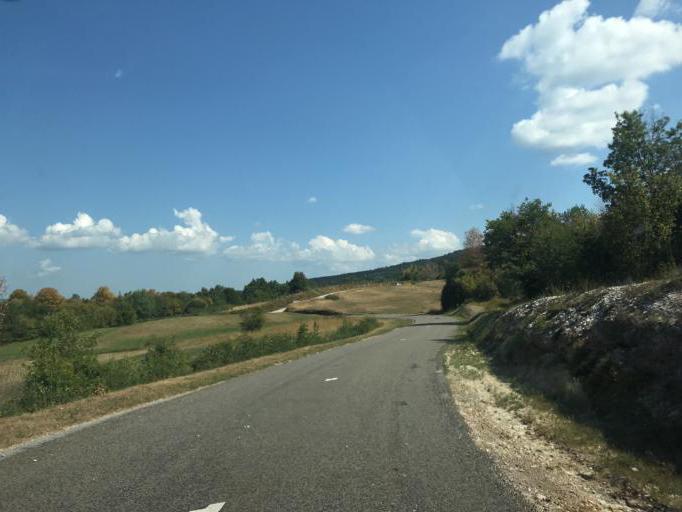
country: FR
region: Franche-Comte
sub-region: Departement du Jura
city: Moirans-en-Montagne
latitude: 46.4631
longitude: 5.7255
